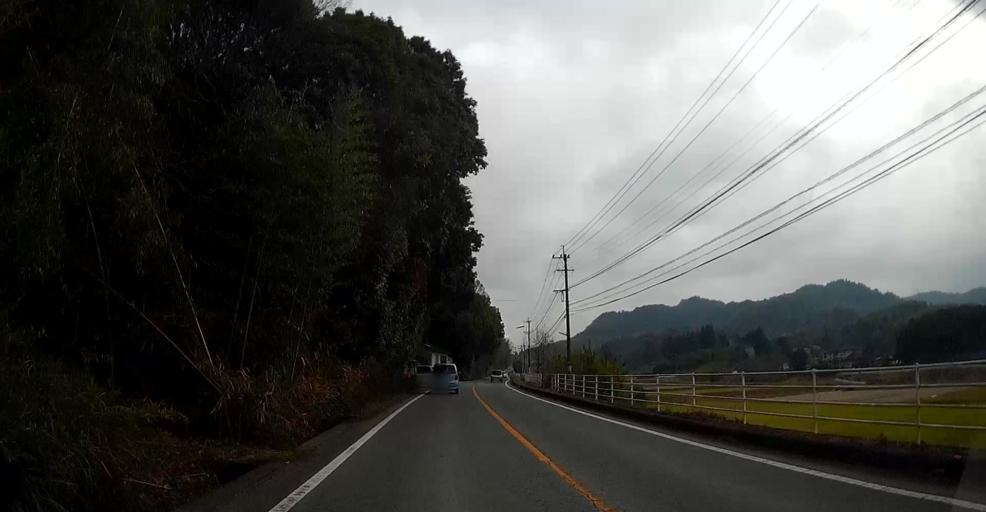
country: JP
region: Kumamoto
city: Matsubase
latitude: 32.6480
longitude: 130.7216
